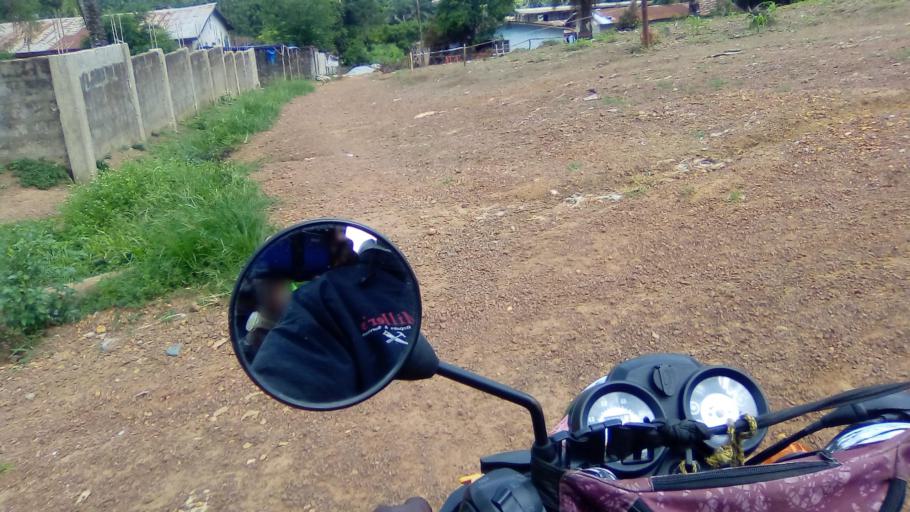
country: SL
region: Southern Province
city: Bo
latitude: 7.9505
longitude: -11.7304
